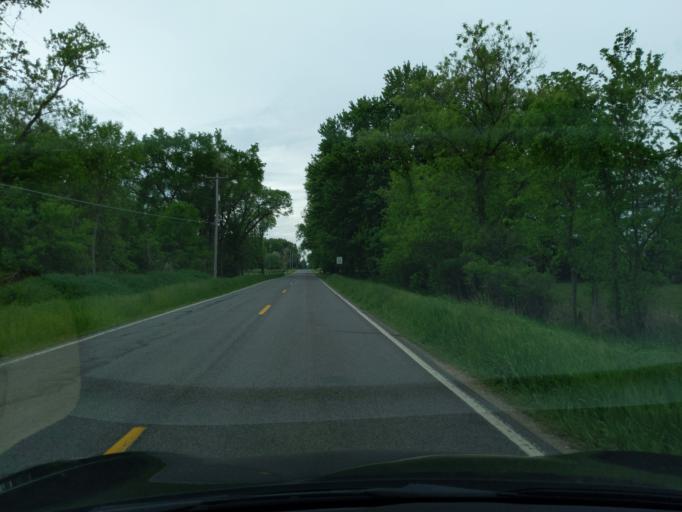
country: US
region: Michigan
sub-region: Ingham County
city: Leslie
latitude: 42.3696
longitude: -84.3491
